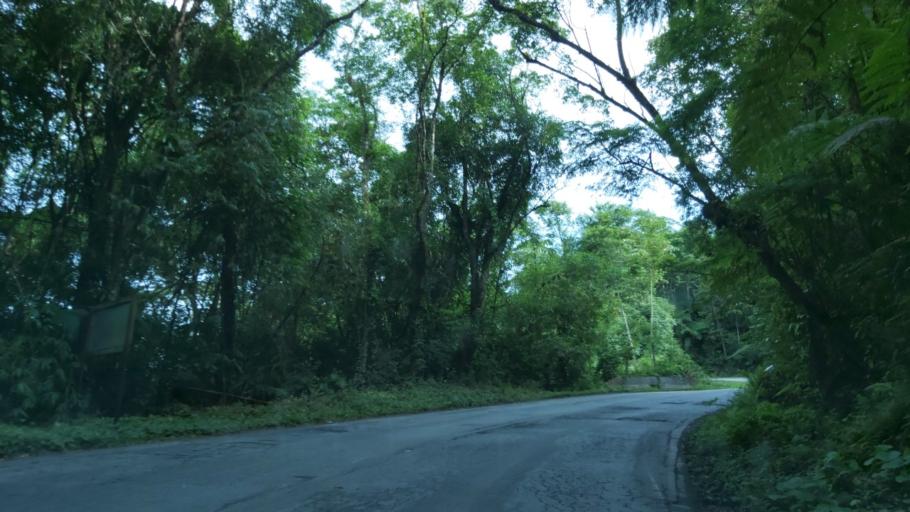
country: BR
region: Sao Paulo
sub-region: Miracatu
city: Miracatu
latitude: -24.0528
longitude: -47.5714
